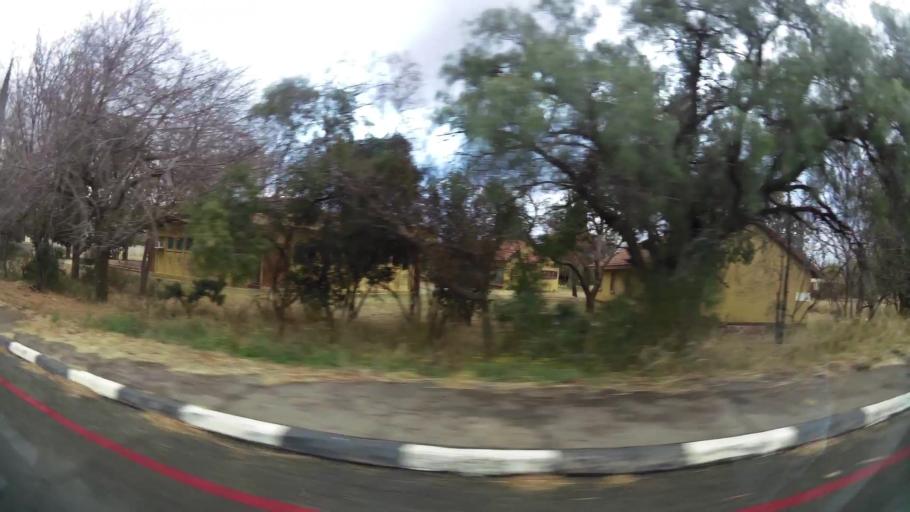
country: ZA
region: Orange Free State
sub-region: Lejweleputswa District Municipality
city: Welkom
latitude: -27.9604
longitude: 26.7258
